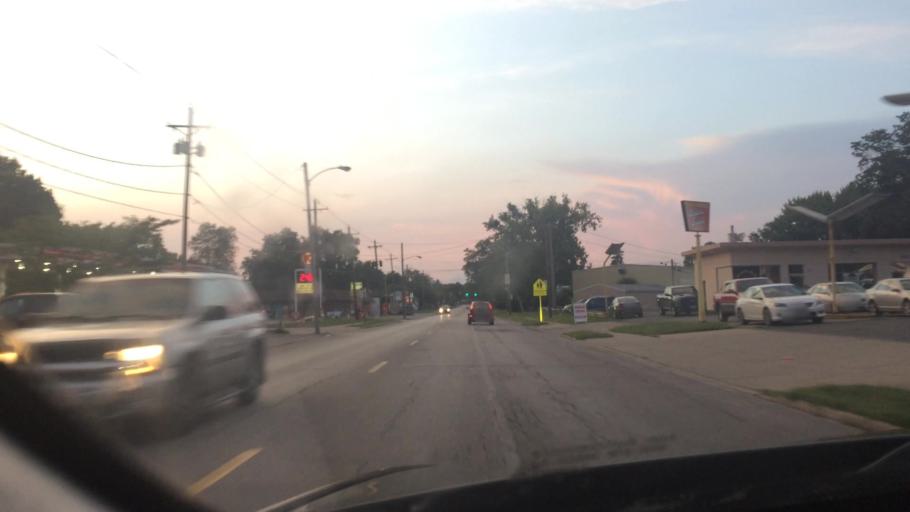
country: US
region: Michigan
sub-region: Monroe County
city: Lambertville
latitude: 41.7158
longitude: -83.6153
